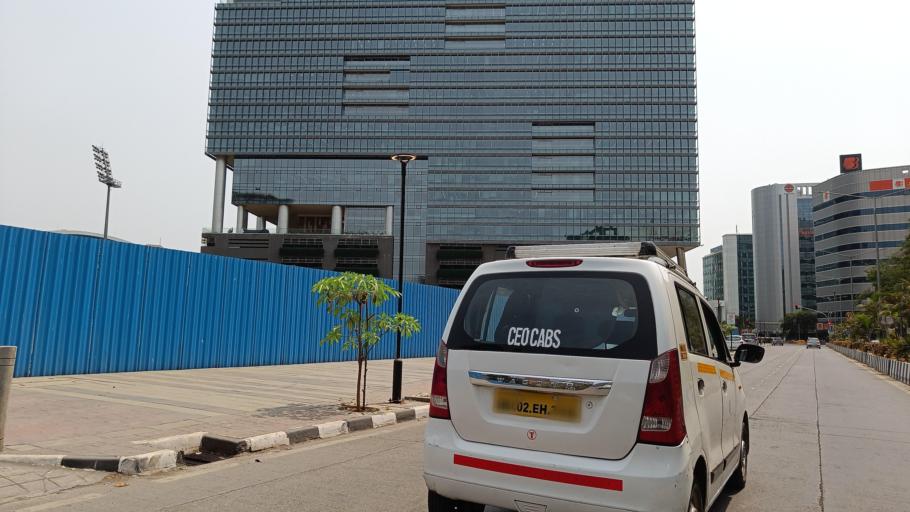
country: IN
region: Maharashtra
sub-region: Mumbai Suburban
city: Mumbai
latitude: 19.0622
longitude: 72.8648
